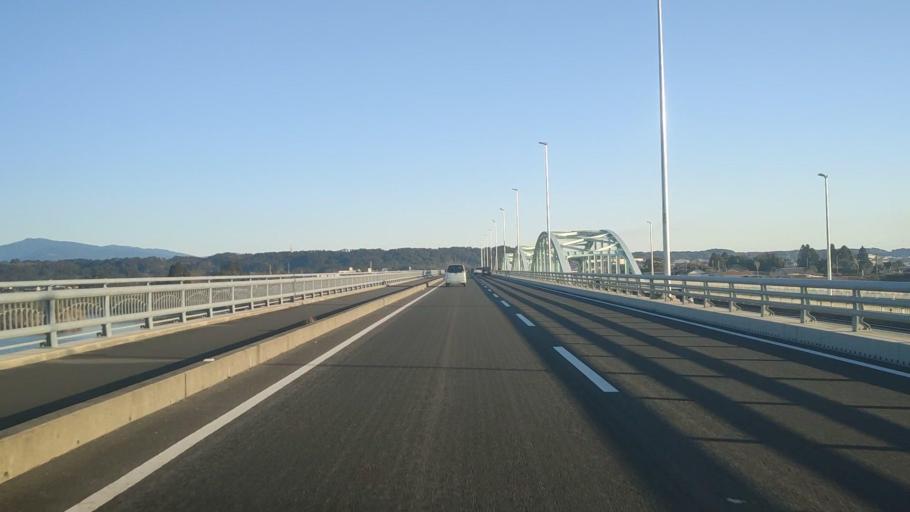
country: JP
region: Miyazaki
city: Tsuma
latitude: 32.0492
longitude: 131.4720
